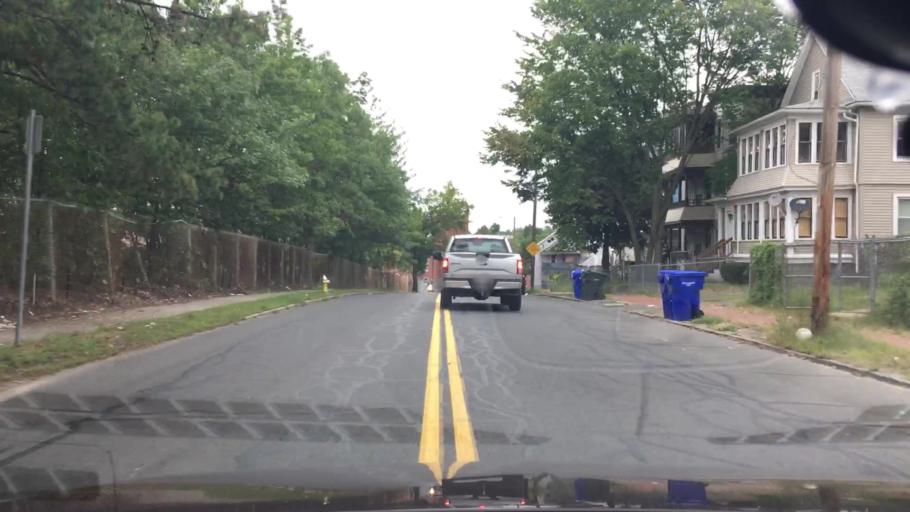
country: US
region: Massachusetts
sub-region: Hampden County
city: Springfield
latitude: 42.0951
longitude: -72.5630
